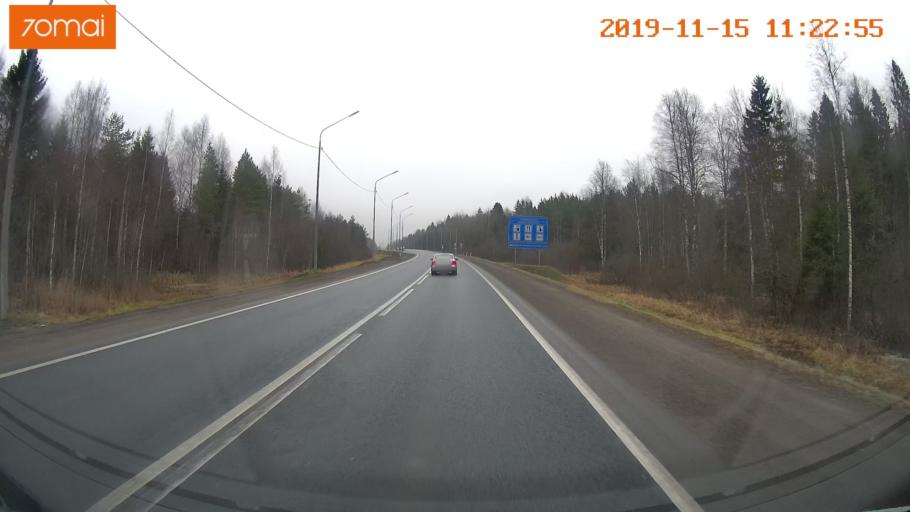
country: RU
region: Vologda
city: Molochnoye
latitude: 59.1485
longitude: 39.3681
